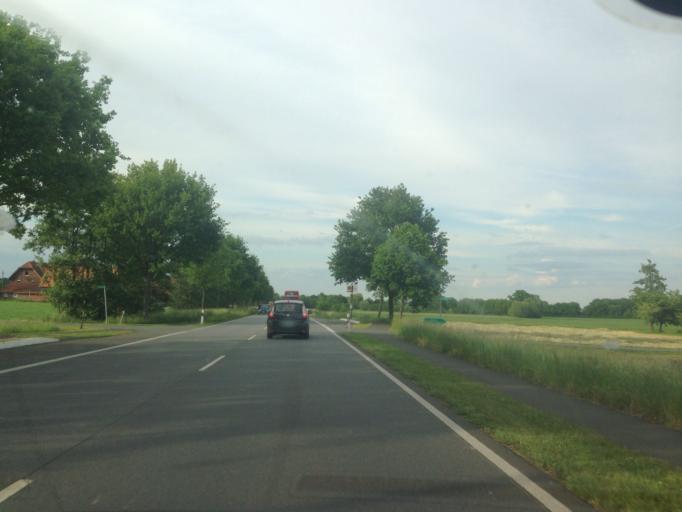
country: DE
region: North Rhine-Westphalia
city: Ludinghausen
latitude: 51.7927
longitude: 7.4690
